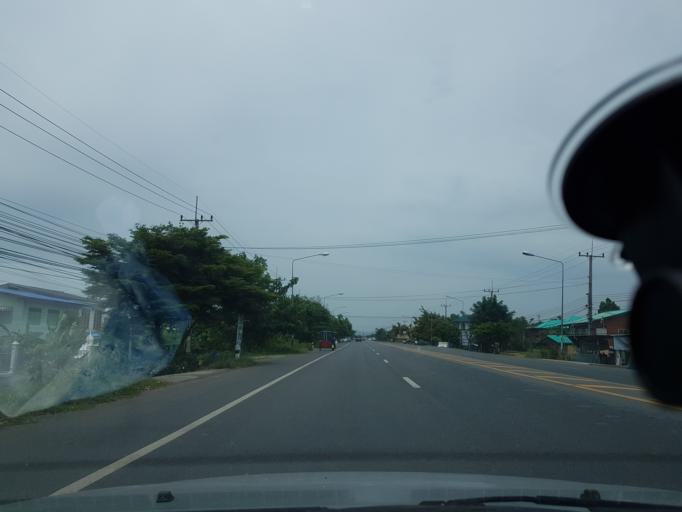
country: TH
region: Lop Buri
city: Lop Buri
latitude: 14.8090
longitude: 100.5835
